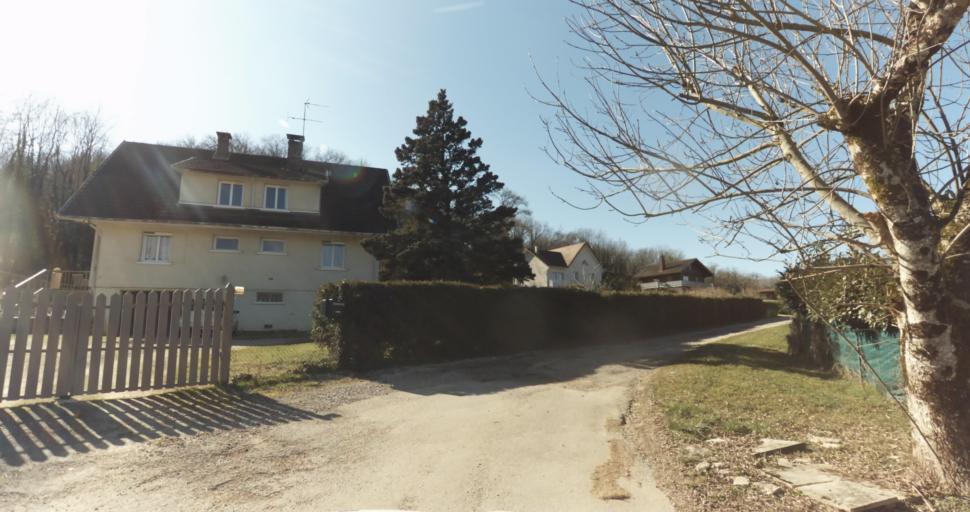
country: FR
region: Franche-Comte
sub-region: Departement du Jura
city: Montmorot
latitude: 46.6735
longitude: 5.5244
